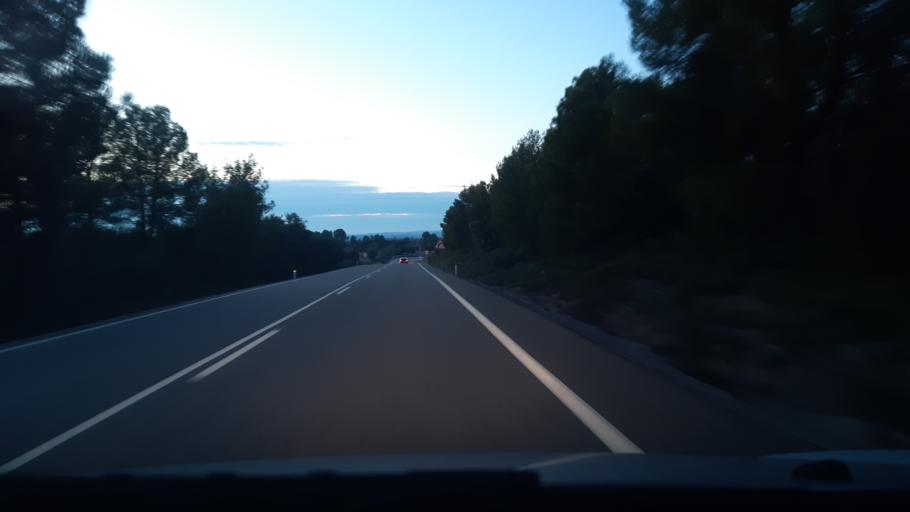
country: ES
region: Aragon
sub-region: Provincia de Teruel
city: Calaceite
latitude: 40.9625
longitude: 0.2113
